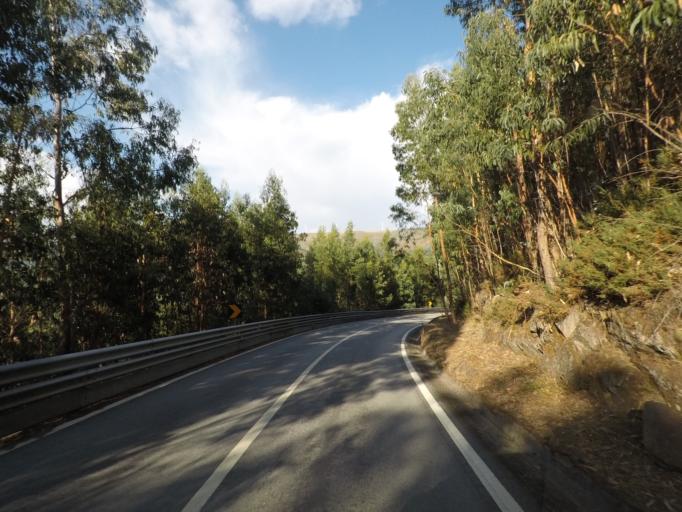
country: PT
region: Vila Real
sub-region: Mesao Frio
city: Mesao Frio
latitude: 41.1758
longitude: -7.9195
